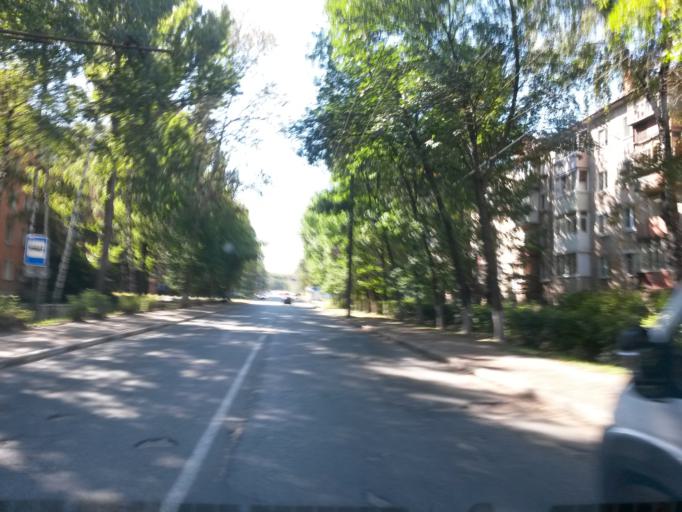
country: RU
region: Jaroslavl
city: Yaroslavl
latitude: 57.5814
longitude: 39.8358
